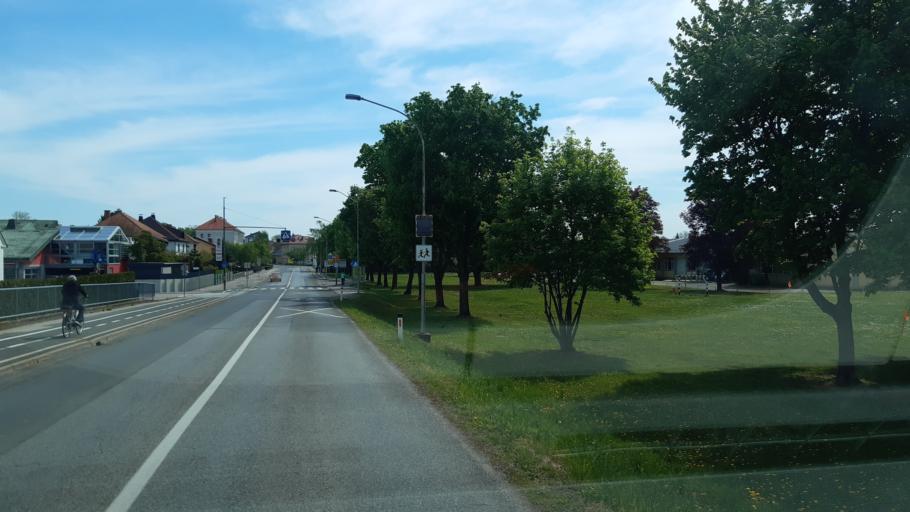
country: SI
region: Murska Sobota
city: Murska Sobota
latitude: 46.6616
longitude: 16.1507
